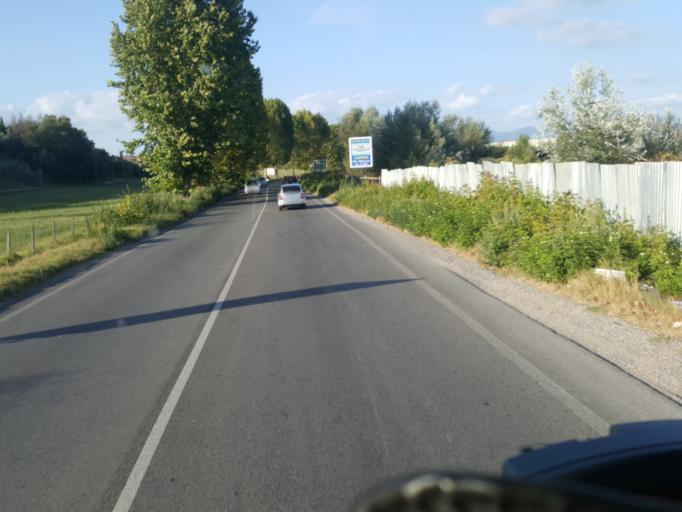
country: IT
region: Latium
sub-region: Citta metropolitana di Roma Capitale
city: Girardi-Bellavista-Terrazze
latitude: 42.1079
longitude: 12.5836
